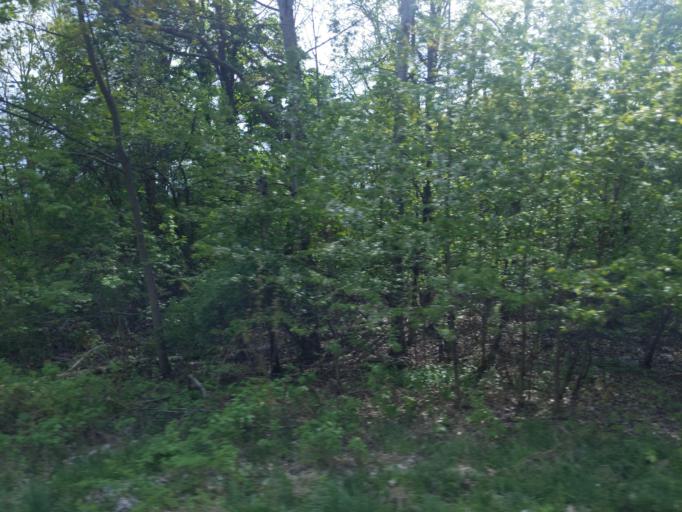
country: DE
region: Saxony
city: Demitz-Thumitz
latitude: 51.1424
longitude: 14.2383
